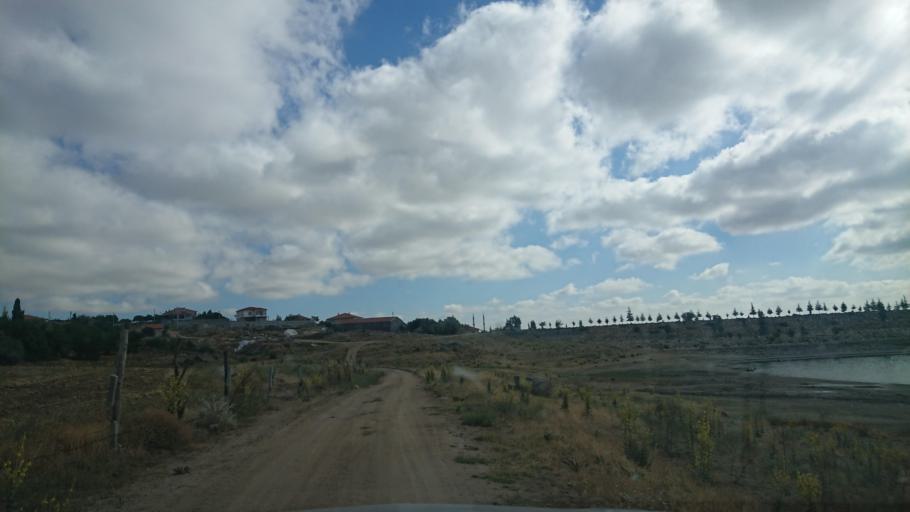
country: TR
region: Aksaray
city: Agacoren
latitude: 38.8648
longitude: 33.9466
